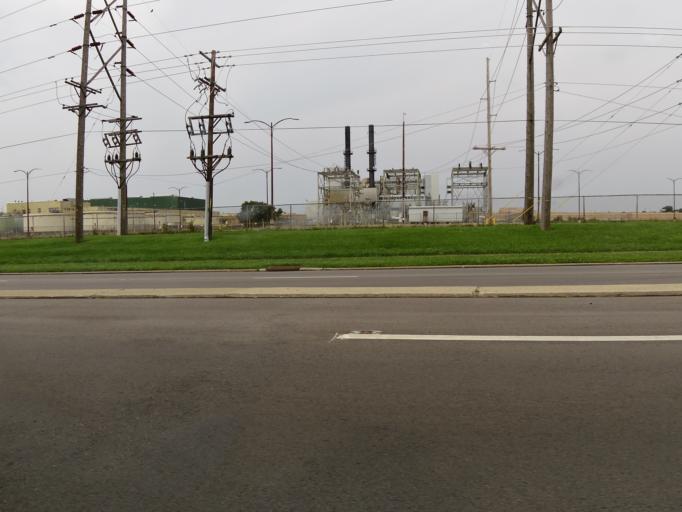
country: US
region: Ohio
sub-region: Montgomery County
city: Kettering
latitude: 39.7112
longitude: -84.1239
